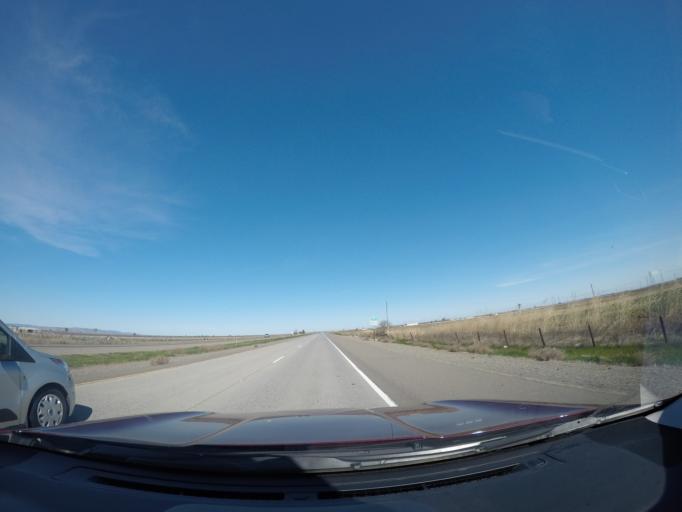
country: US
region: California
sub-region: Yolo County
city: Cottonwood
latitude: 38.6489
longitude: -121.9518
